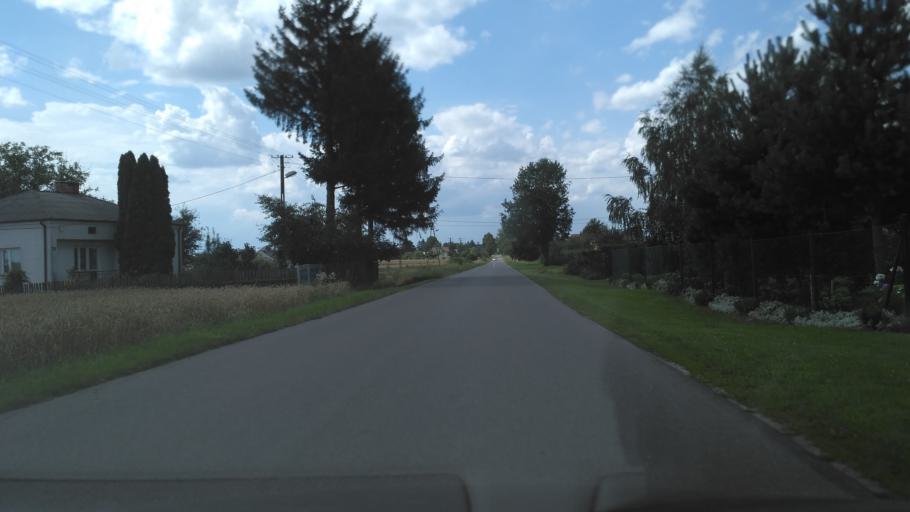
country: PL
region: Lublin Voivodeship
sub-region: Powiat swidnicki
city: Trawniki
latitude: 51.1808
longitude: 22.9593
